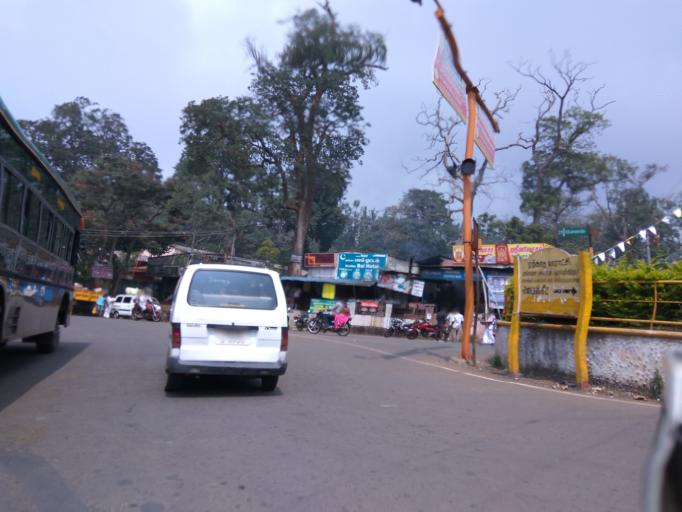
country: IN
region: Tamil Nadu
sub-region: Salem
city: Salem
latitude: 11.7854
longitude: 78.2110
